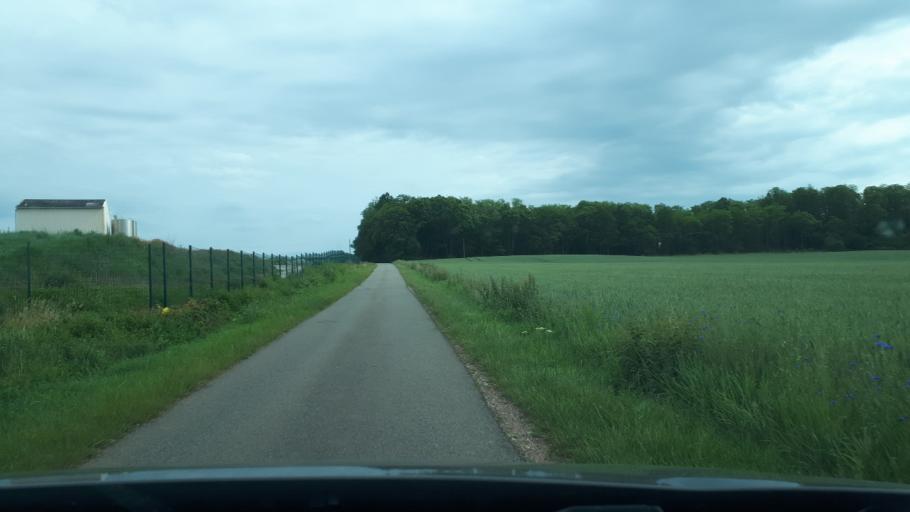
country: FR
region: Centre
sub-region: Departement du Cher
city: Sancerre
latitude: 47.3137
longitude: 2.7422
